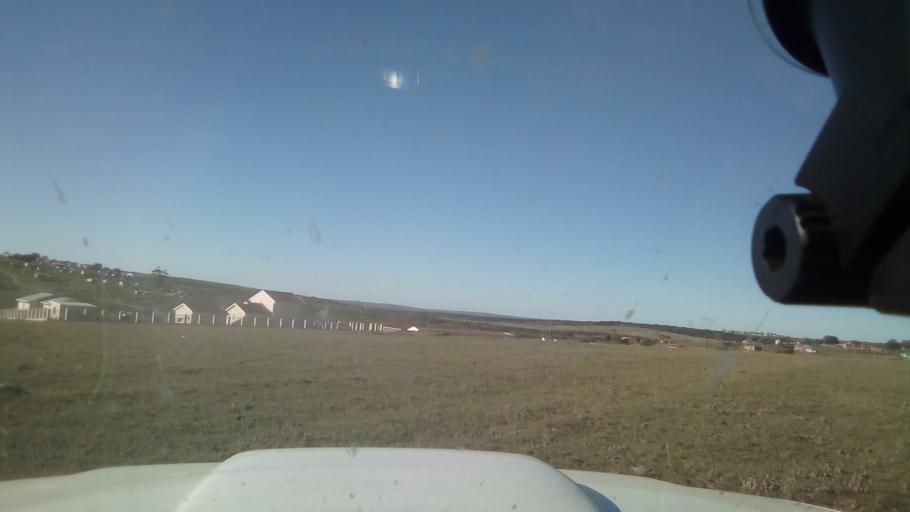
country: ZA
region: Eastern Cape
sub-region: Buffalo City Metropolitan Municipality
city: Bhisho
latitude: -32.9475
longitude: 27.2850
